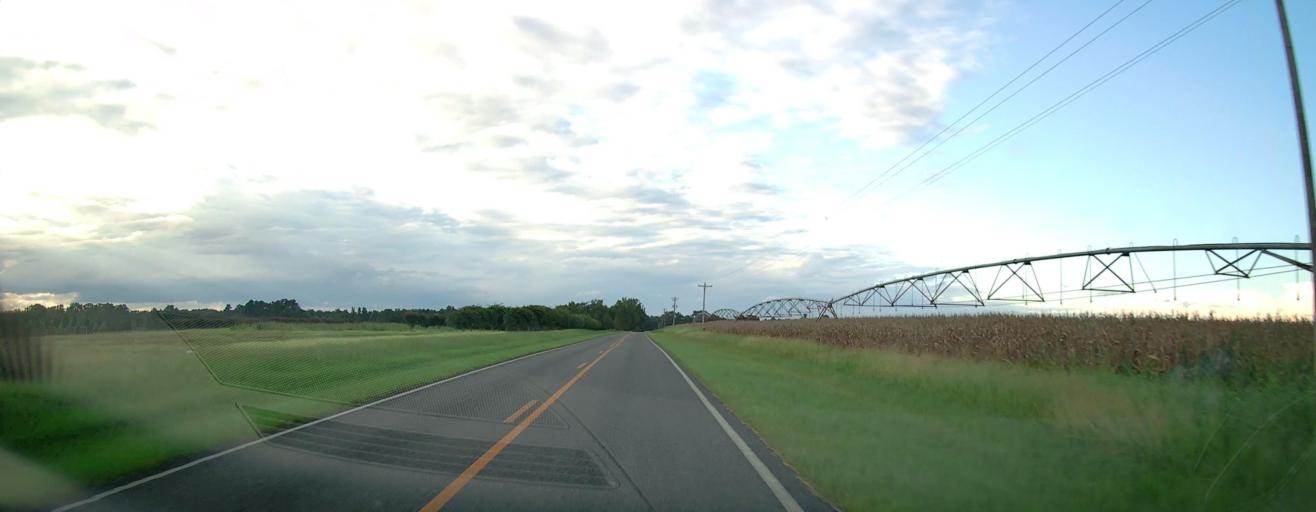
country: US
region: Georgia
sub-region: Pulaski County
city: Hawkinsville
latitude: 32.3029
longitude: -83.5529
